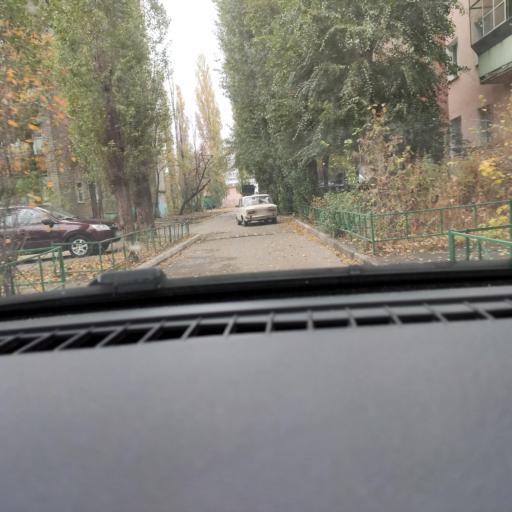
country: RU
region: Voronezj
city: Voronezh
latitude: 51.6896
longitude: 39.2580
